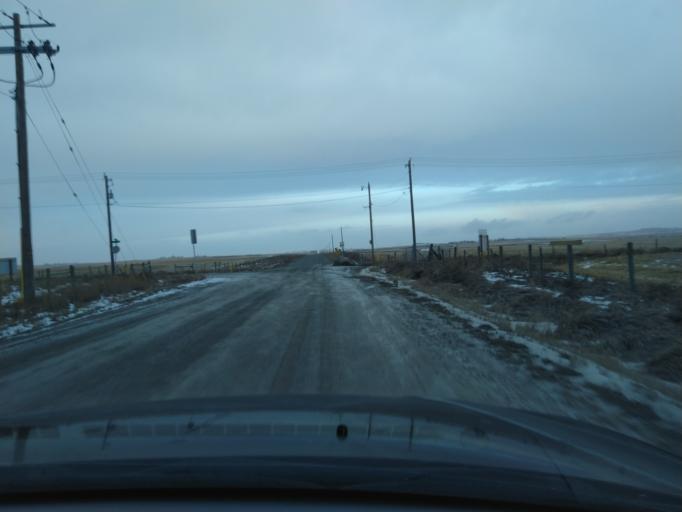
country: CA
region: Alberta
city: Airdrie
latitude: 51.1830
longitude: -114.0248
